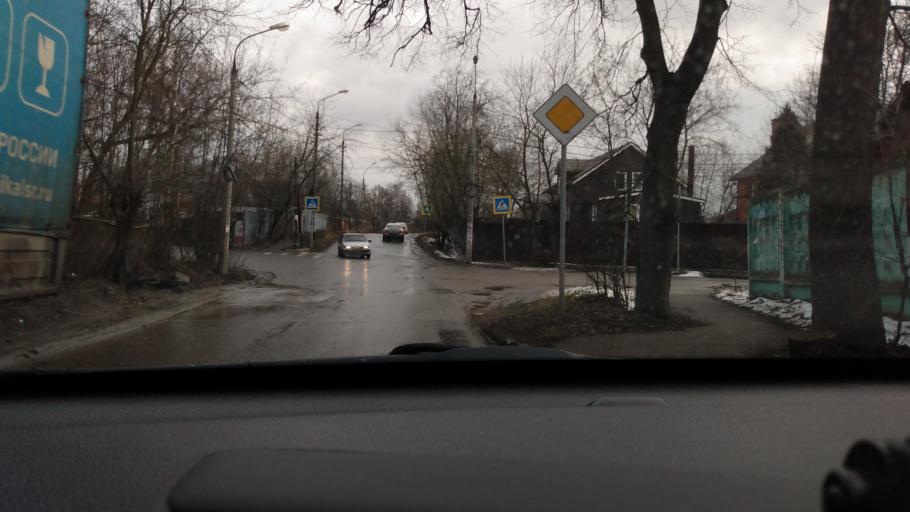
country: RU
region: Moskovskaya
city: Yubileyny
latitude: 55.9290
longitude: 37.8647
